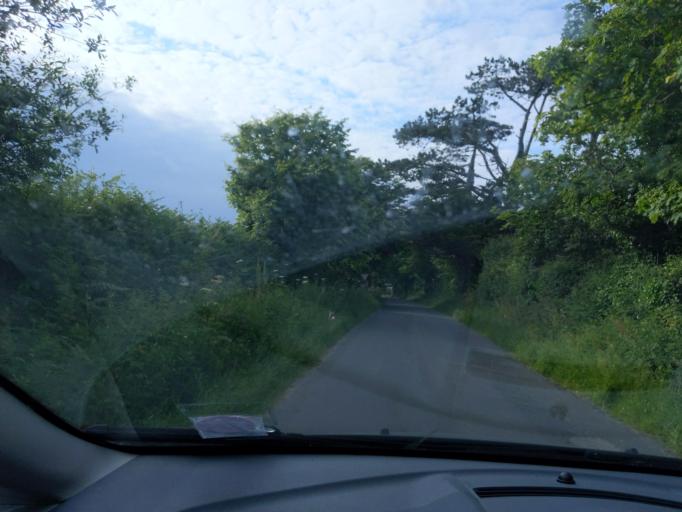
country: IM
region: Ramsey
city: Ramsey
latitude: 54.3471
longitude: -4.4484
